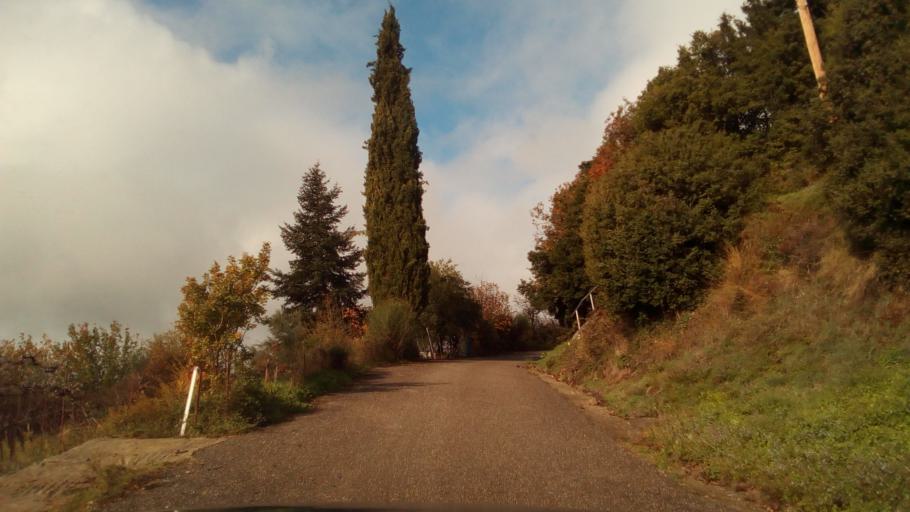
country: GR
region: West Greece
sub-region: Nomos Aitolias kai Akarnanias
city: Nafpaktos
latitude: 38.5157
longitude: 21.9551
